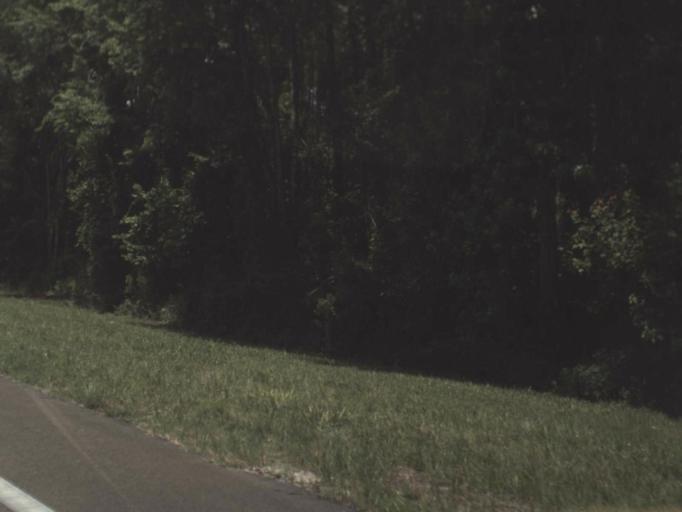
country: US
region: Florida
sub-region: Union County
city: Lake Butler
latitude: 29.9076
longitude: -82.4229
